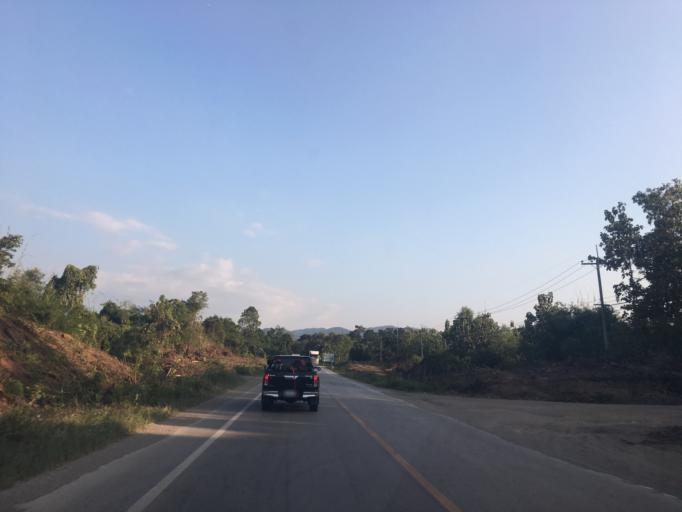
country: TH
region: Lampang
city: Ngao
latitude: 18.6168
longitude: 100.0246
